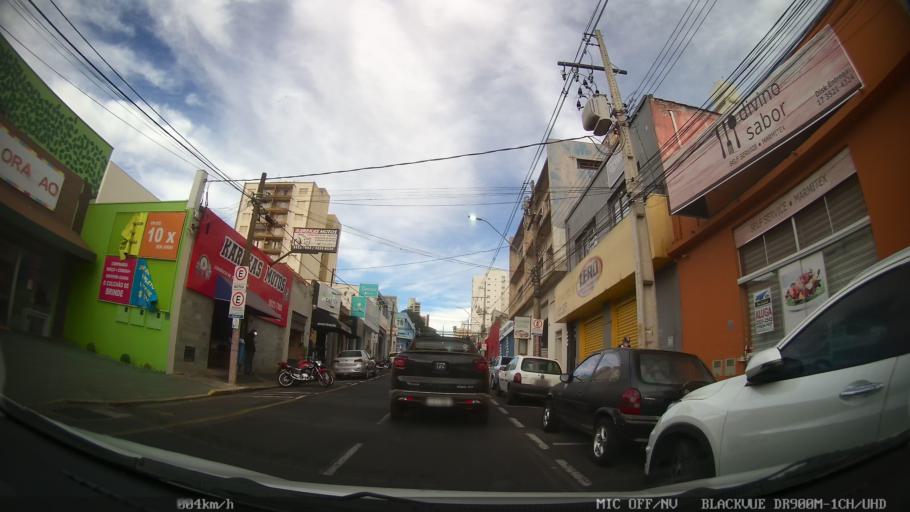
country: BR
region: Sao Paulo
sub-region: Catanduva
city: Catanduva
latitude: -21.1335
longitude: -48.9723
